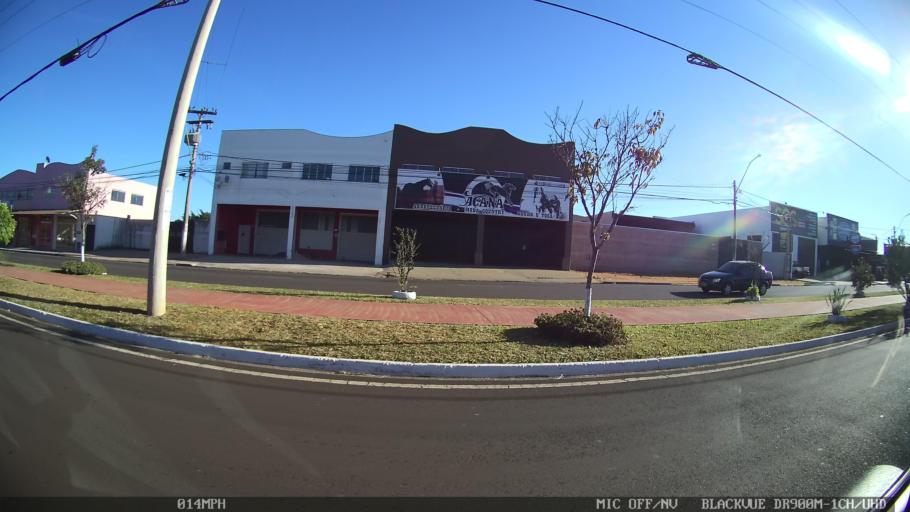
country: BR
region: Sao Paulo
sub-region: Franca
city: Franca
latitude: -20.5727
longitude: -47.3707
